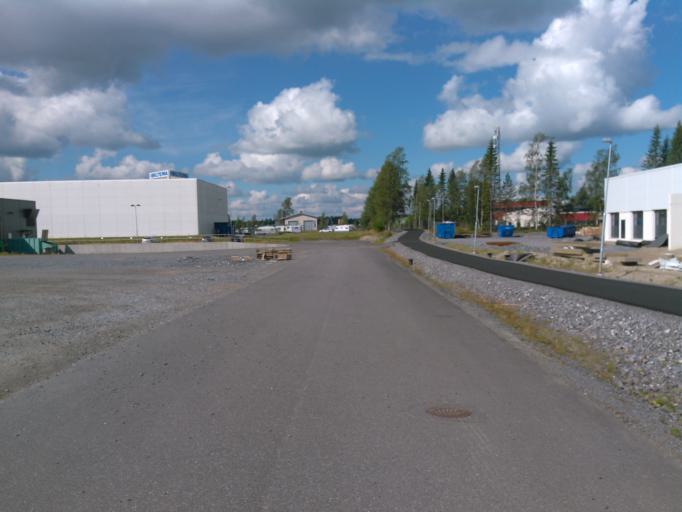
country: SE
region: Vaesterbotten
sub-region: Umea Kommun
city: Ersmark
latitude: 63.8498
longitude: 20.3211
